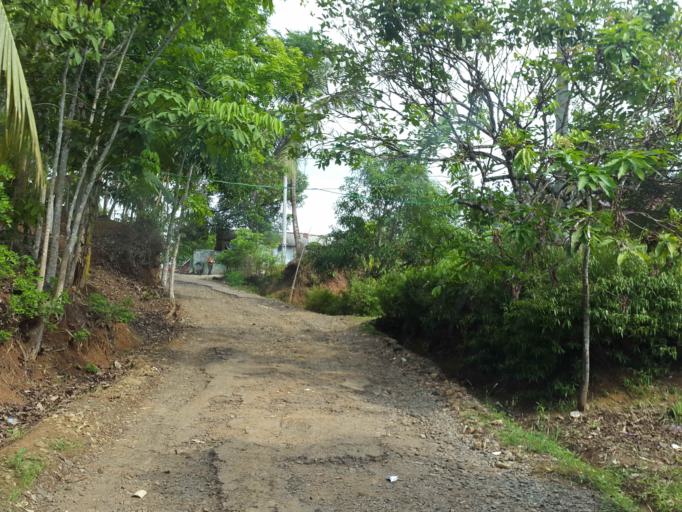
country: ID
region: Central Java
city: Cimalati
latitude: -7.3178
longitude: 108.6604
